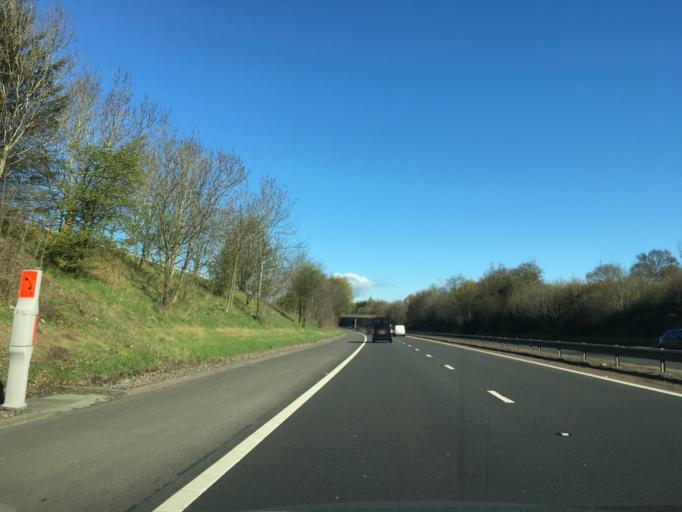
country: GB
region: Scotland
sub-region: Stirling
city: Stirling
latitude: 56.1024
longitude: -3.9537
